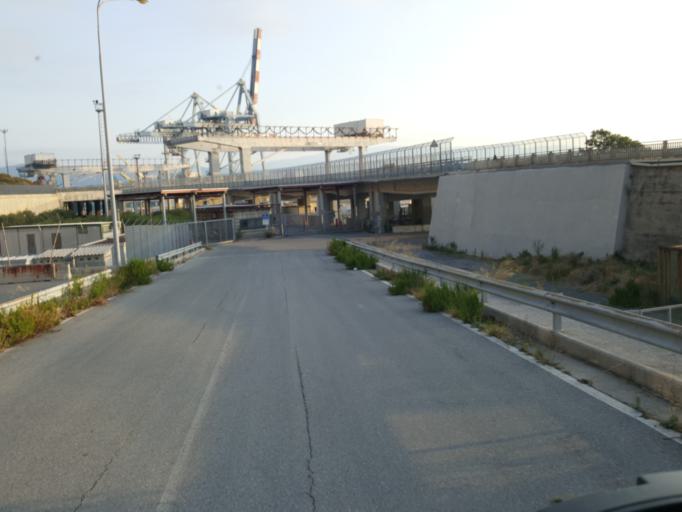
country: IT
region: Liguria
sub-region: Provincia di Savona
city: Bergeggi
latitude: 44.2584
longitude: 8.4525
